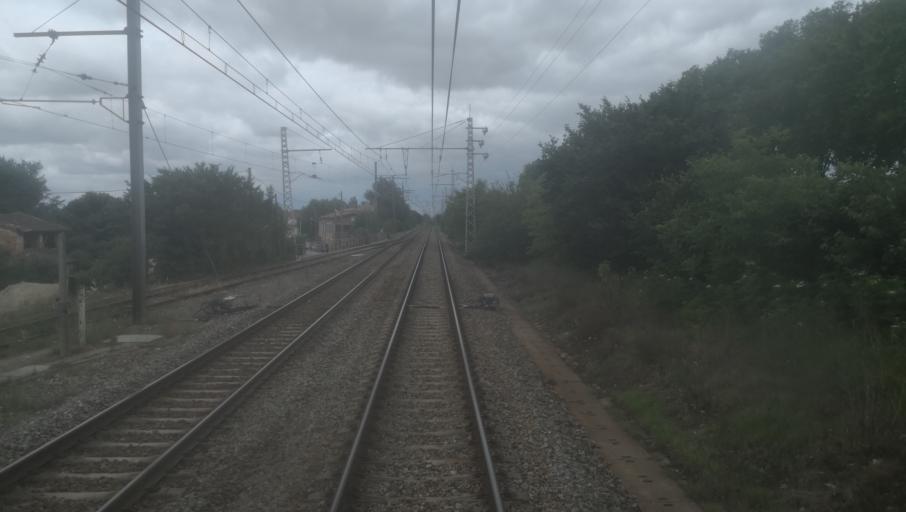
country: FR
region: Midi-Pyrenees
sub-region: Departement de la Haute-Garonne
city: Baziege
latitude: 43.4542
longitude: 1.6194
